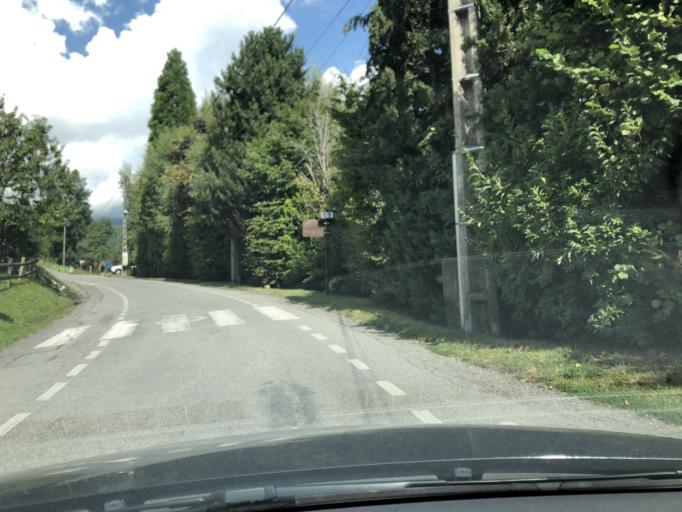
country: FR
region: Rhone-Alpes
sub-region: Departement de la Haute-Savoie
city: Combloux
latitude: 45.8950
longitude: 6.6474
